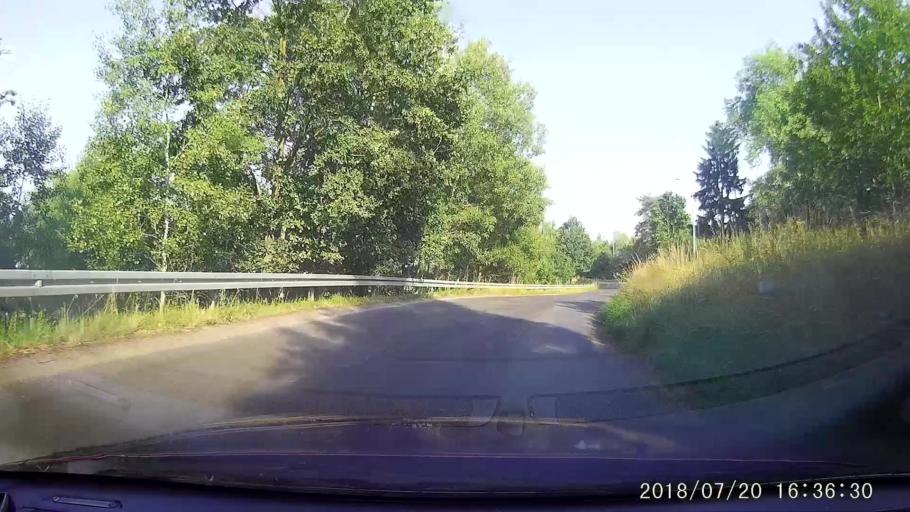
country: PL
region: Lower Silesian Voivodeship
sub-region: Powiat zgorzelecki
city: Sulikow
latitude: 51.0797
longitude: 15.1111
